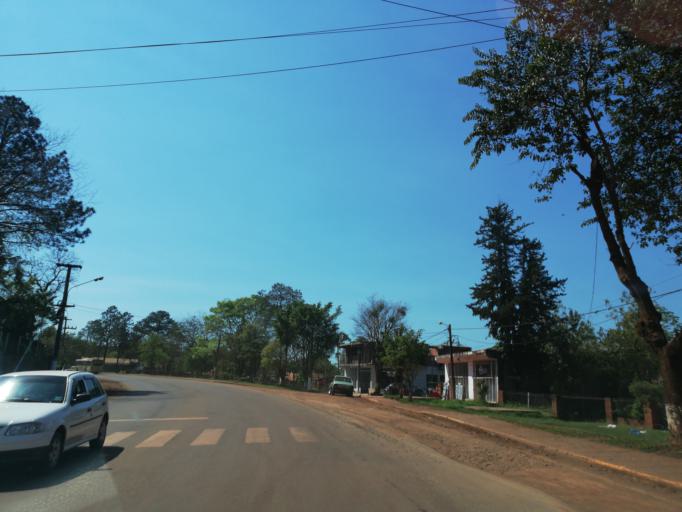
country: AR
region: Misiones
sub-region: Departamento de Eldorado
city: Eldorado
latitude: -26.4071
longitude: -54.6529
